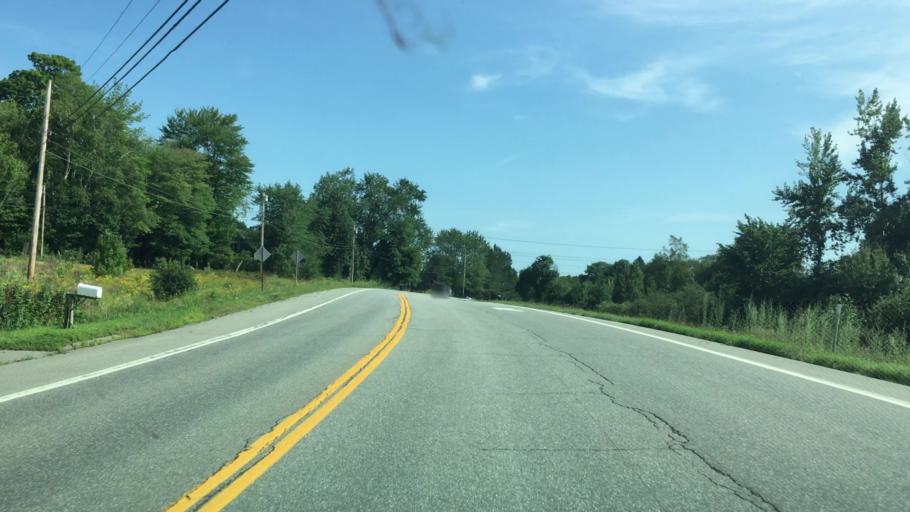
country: US
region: Maine
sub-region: Penobscot County
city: Orrington
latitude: 44.6886
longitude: -68.8472
